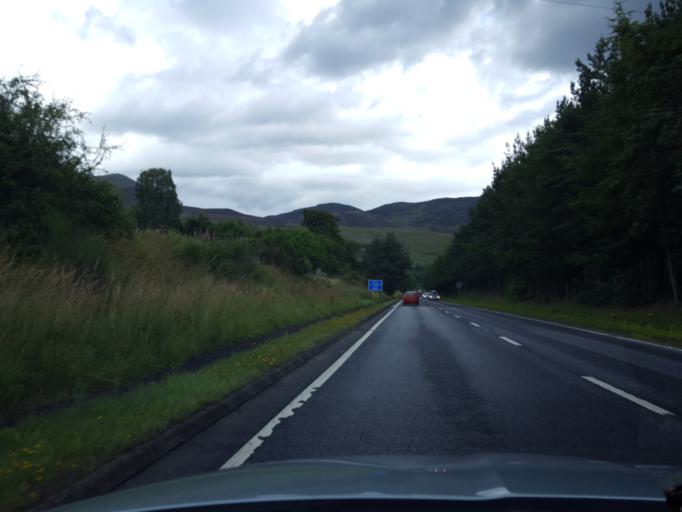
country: GB
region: Scotland
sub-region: Perth and Kinross
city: Pitlochry
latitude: 56.7514
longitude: -3.7869
